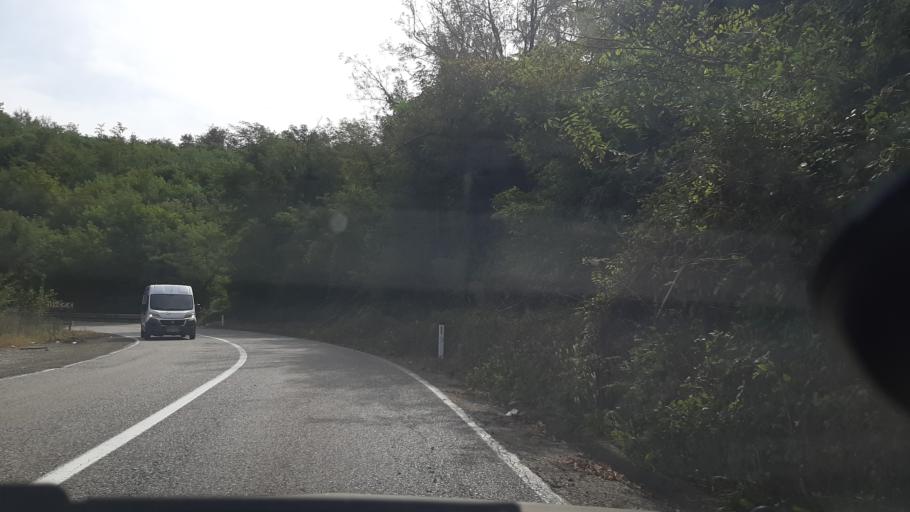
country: BA
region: Republika Srpska
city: Laktasi
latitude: 44.8737
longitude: 17.3622
